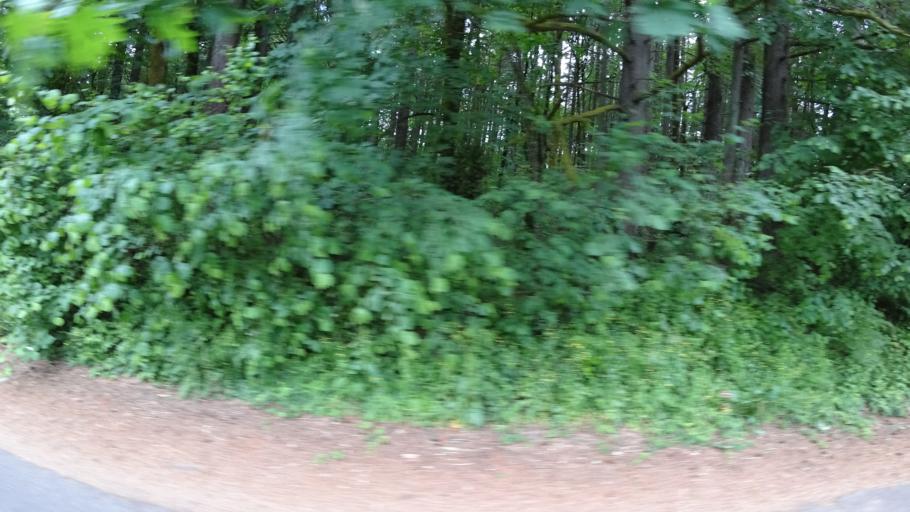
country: US
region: Oregon
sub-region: Clackamas County
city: Lake Oswego
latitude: 45.4494
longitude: -122.7025
